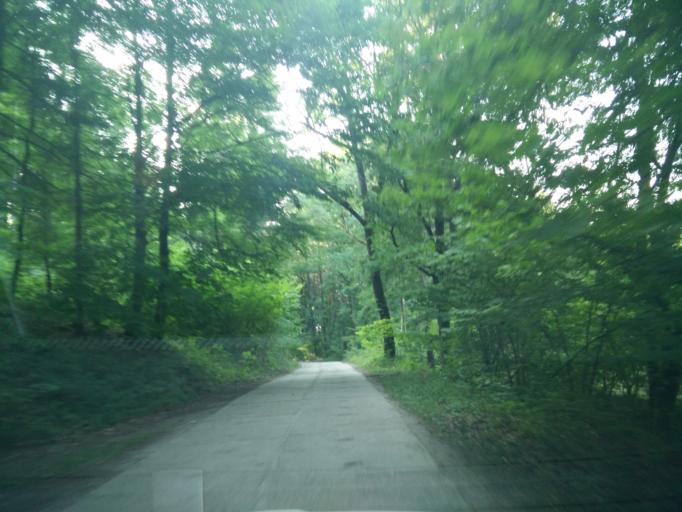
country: SK
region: Nitriansky
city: Prievidza
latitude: 48.7474
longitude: 18.6795
